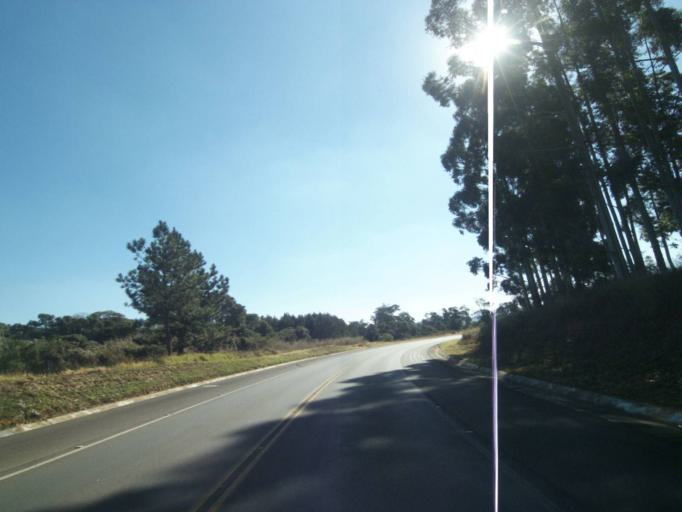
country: BR
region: Parana
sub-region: Tibagi
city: Tibagi
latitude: -24.7891
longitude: -50.4693
